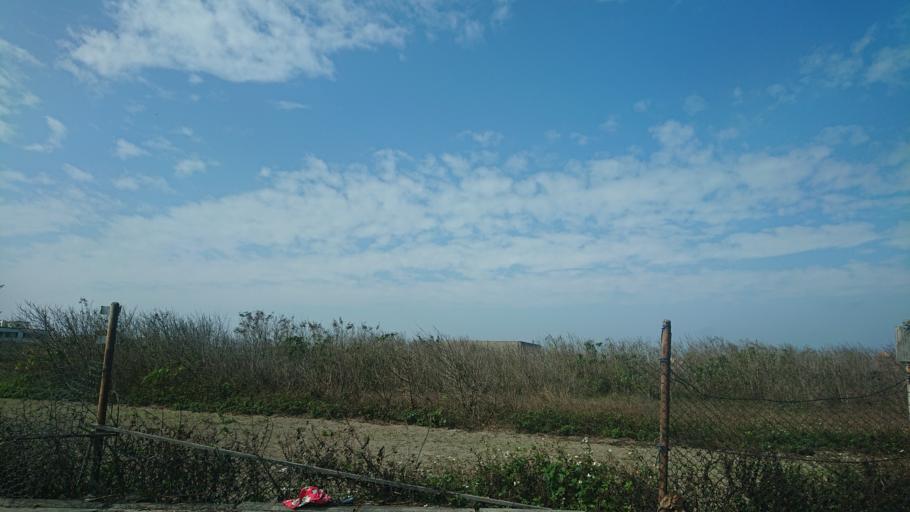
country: TW
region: Taiwan
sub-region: Changhua
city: Chang-hua
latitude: 23.9266
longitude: 120.3225
